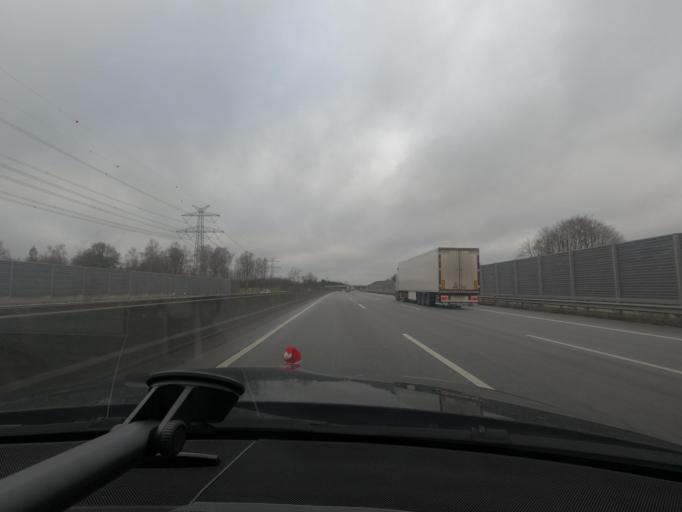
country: DE
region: Schleswig-Holstein
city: Kaltenkirchen
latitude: 53.8206
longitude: 9.9233
